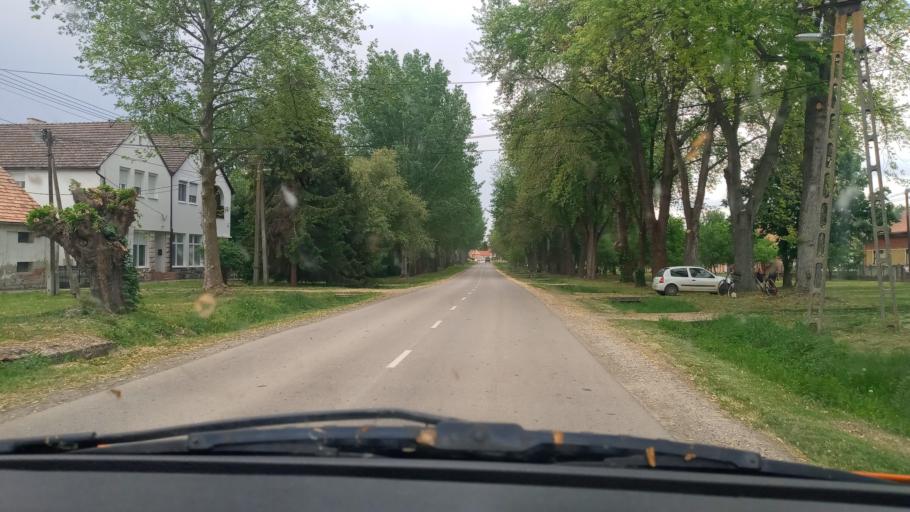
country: HU
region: Baranya
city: Villany
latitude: 45.8424
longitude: 18.4910
